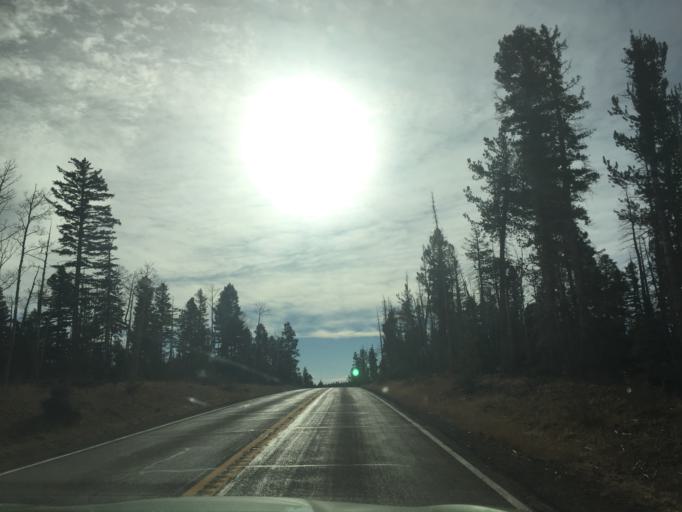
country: US
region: Utah
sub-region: Iron County
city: Parowan
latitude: 37.5308
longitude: -112.7662
